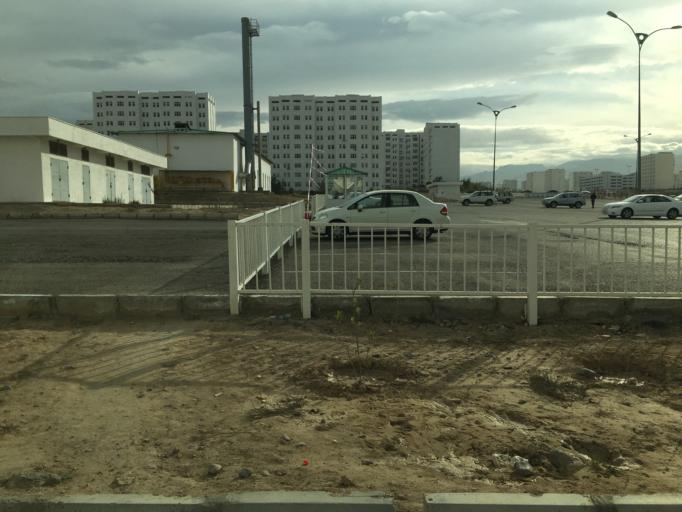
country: TM
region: Ahal
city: Ashgabat
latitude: 37.8986
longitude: 58.4162
